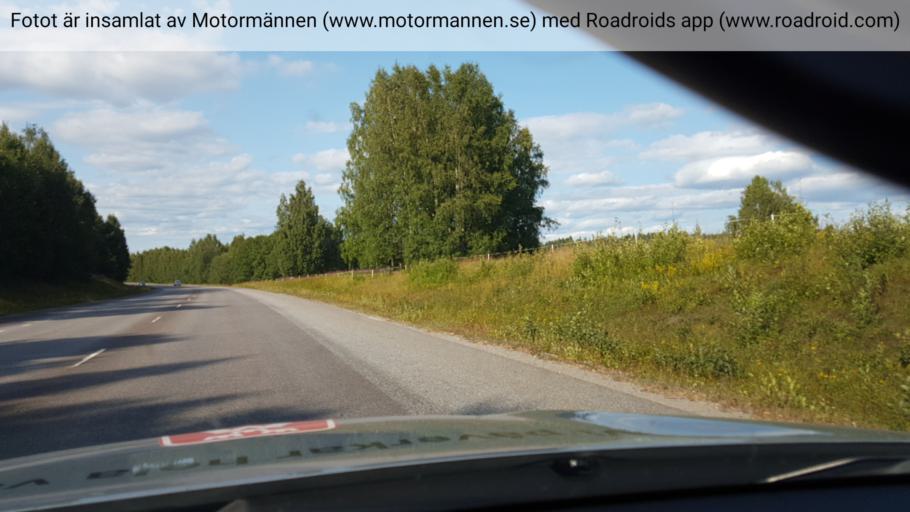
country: SE
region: Norrbotten
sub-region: Pitea Kommun
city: Pitea
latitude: 65.3014
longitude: 21.5104
